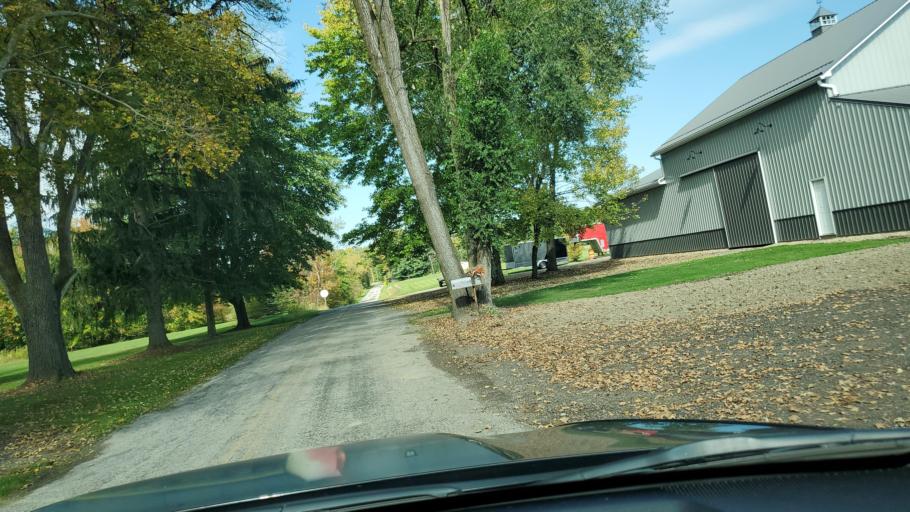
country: US
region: Ohio
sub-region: Trumbull County
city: Cortland
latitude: 41.4089
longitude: -80.6310
